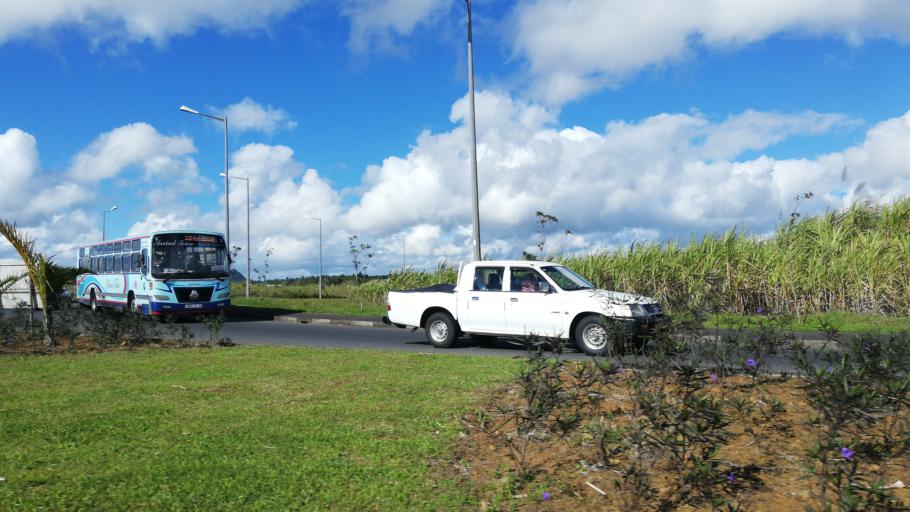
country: MU
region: Moka
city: Quartier Militaire
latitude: -20.2454
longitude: 57.5897
